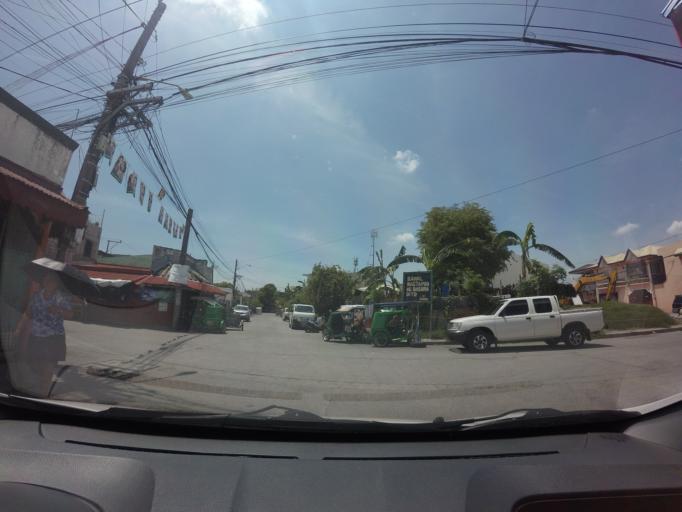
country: PH
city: Sambayanihan People's Village
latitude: 14.4225
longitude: 121.0097
